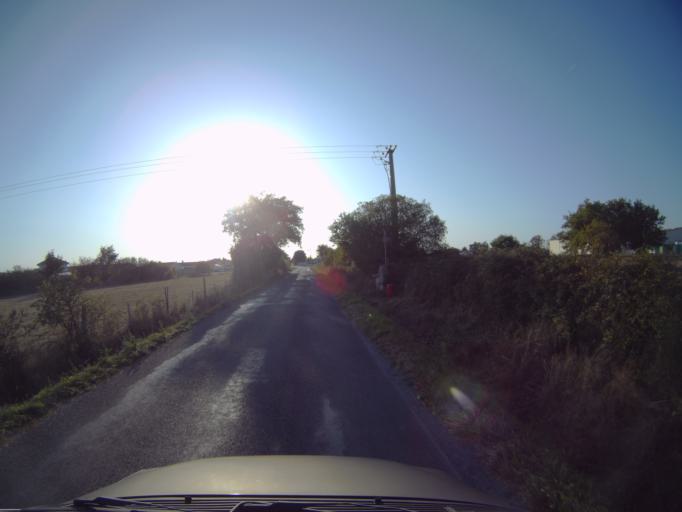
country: FR
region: Pays de la Loire
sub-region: Departement de la Loire-Atlantique
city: Getigne
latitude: 47.0743
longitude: -1.2364
